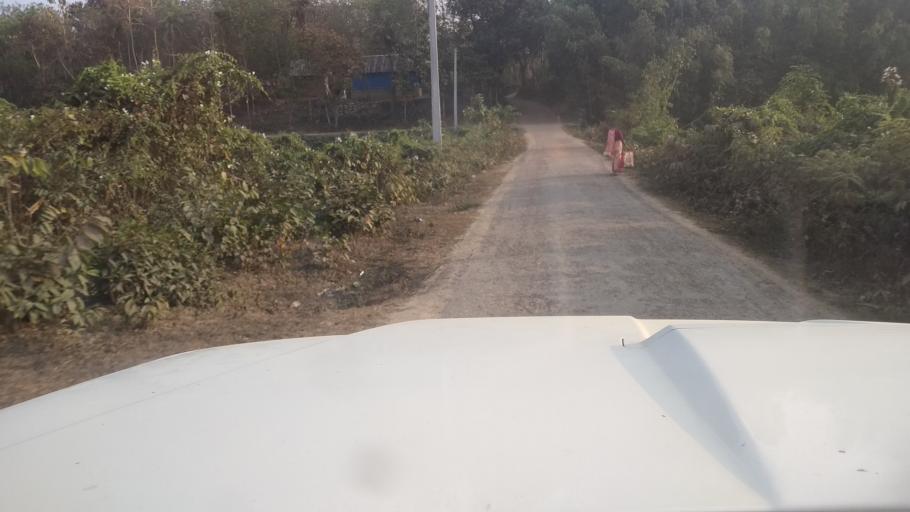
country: IN
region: Tripura
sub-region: West Tripura
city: Sonamura
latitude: 23.3264
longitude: 91.3025
